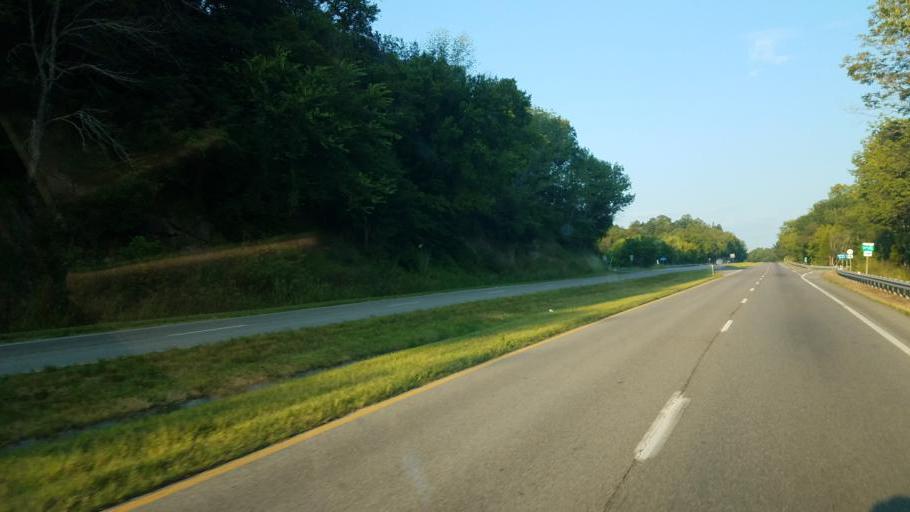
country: US
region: Tennessee
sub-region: Hawkins County
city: Mount Carmel
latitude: 36.6414
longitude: -82.7199
